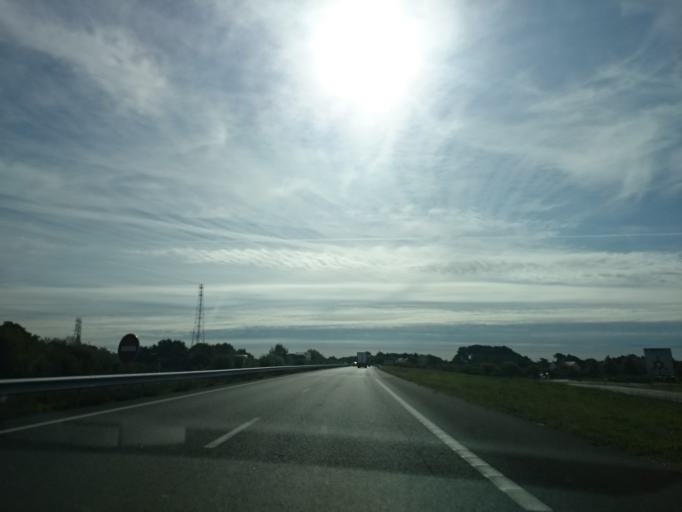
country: FR
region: Brittany
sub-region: Departement du Morbihan
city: Marzan
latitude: 47.5328
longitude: -2.3319
